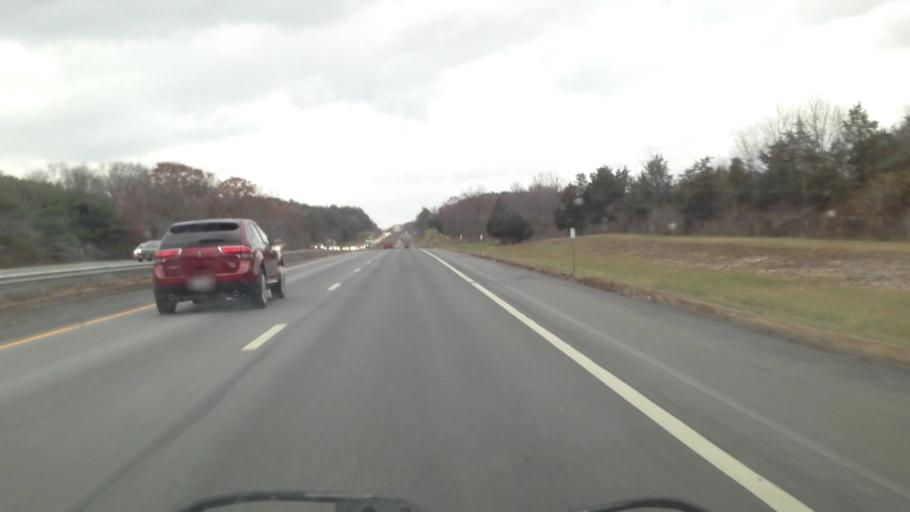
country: US
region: New York
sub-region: Greene County
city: Jefferson Heights
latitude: 42.1751
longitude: -73.9303
